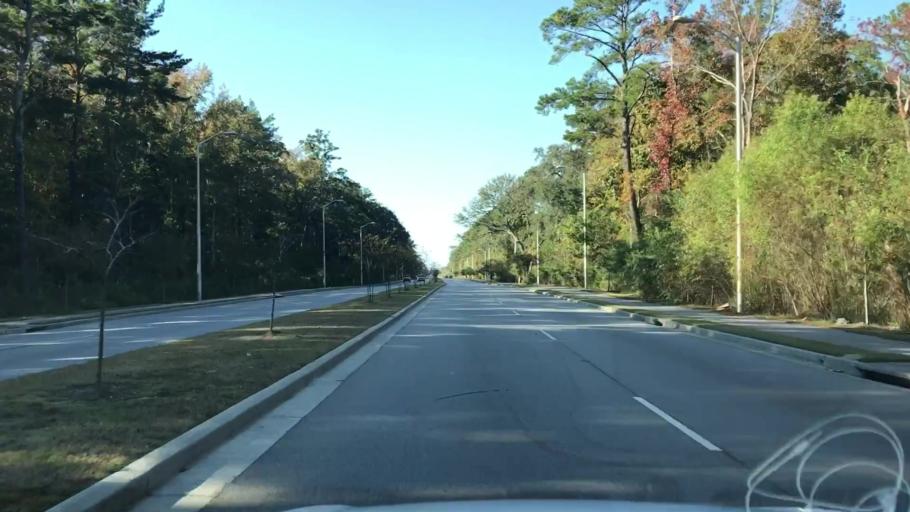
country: US
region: South Carolina
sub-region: Charleston County
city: Shell Point
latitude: 32.8188
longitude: -80.0939
